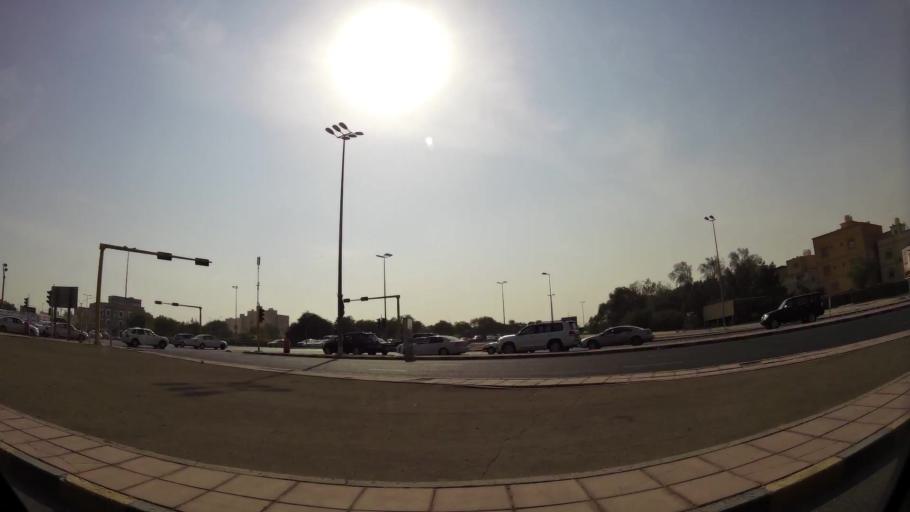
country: KW
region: Al Ahmadi
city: Ar Riqqah
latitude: 29.1572
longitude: 48.0863
